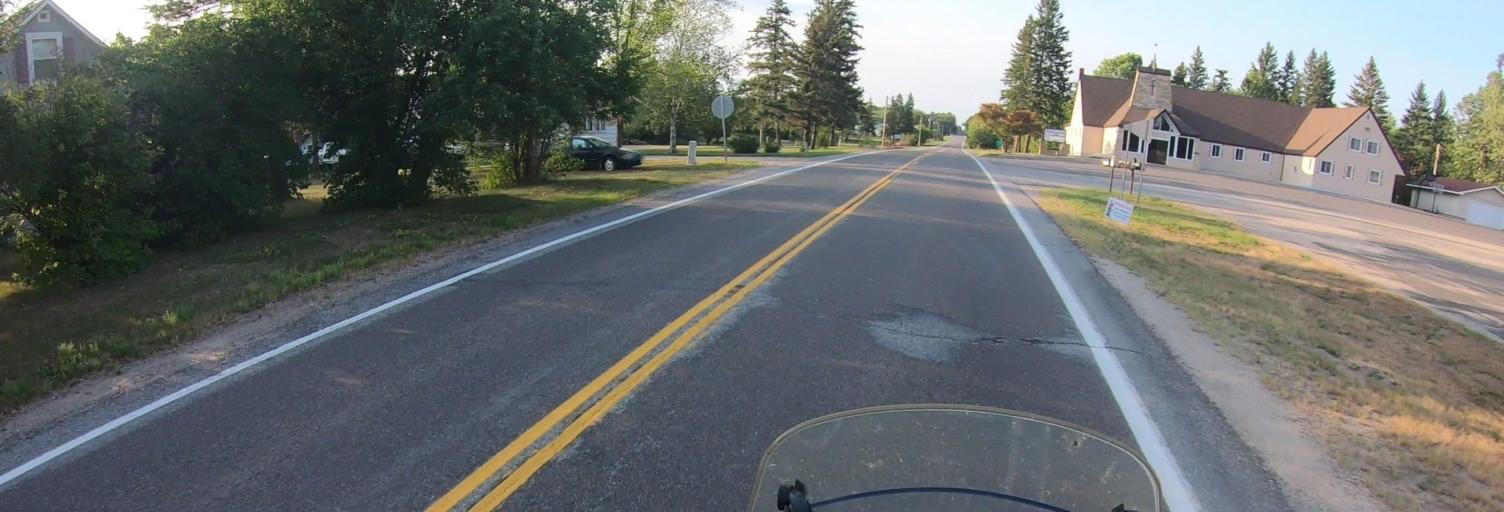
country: US
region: Minnesota
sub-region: Saint Louis County
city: Mountain Iron
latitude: 47.8550
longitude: -92.6831
